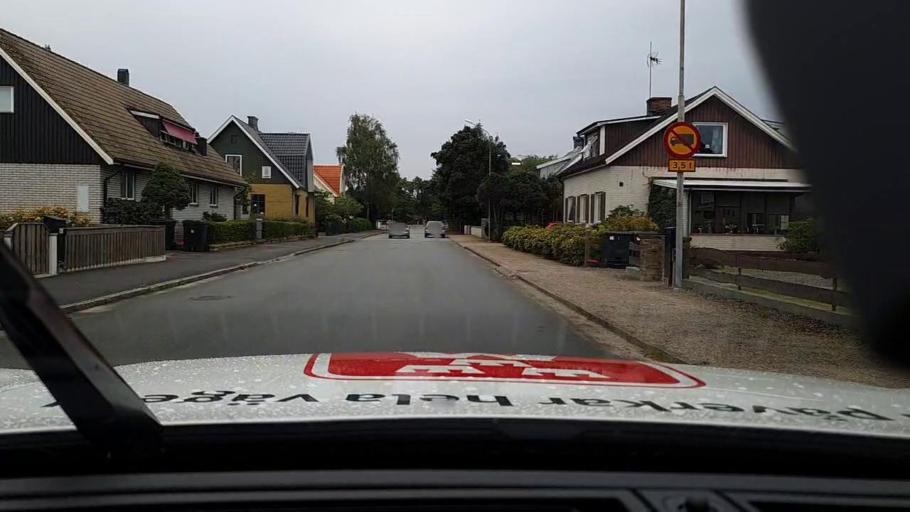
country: SE
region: Skane
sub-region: Hassleholms Kommun
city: Hassleholm
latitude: 56.1645
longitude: 13.7736
